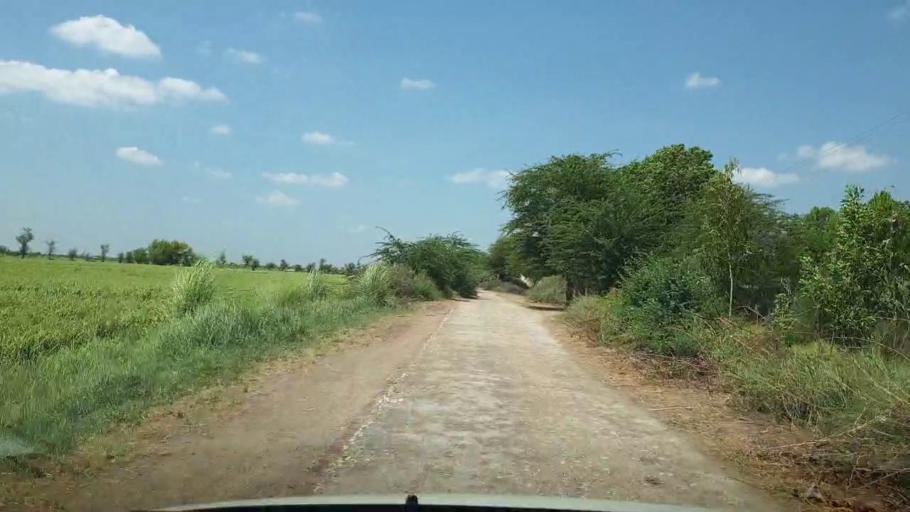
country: PK
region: Sindh
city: Sanghar
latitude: 26.0693
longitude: 69.0478
